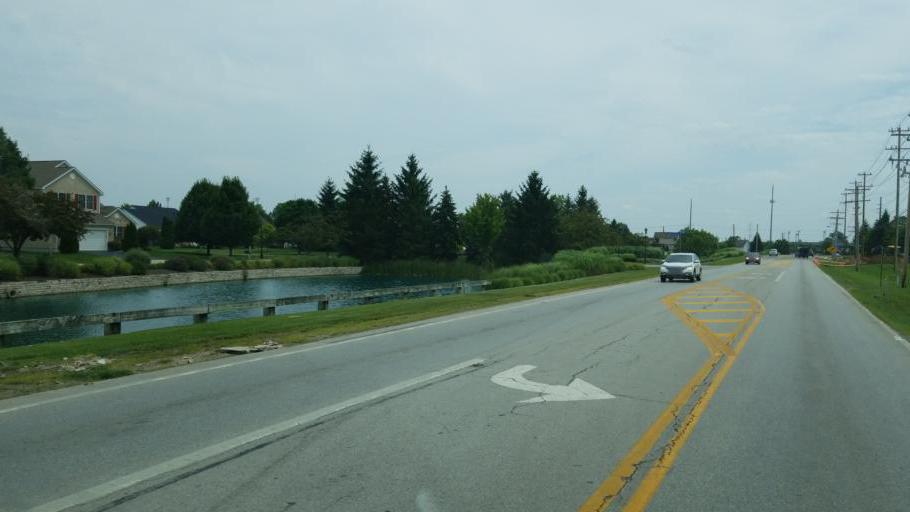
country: US
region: Ohio
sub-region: Franklin County
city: Hilliard
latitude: 40.0331
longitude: -83.1741
